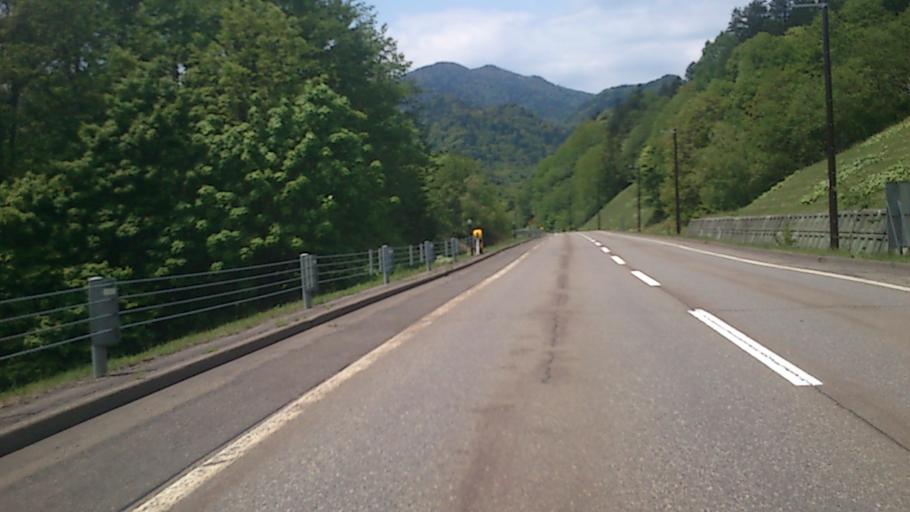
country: JP
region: Hokkaido
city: Otofuke
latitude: 43.3706
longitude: 143.1983
